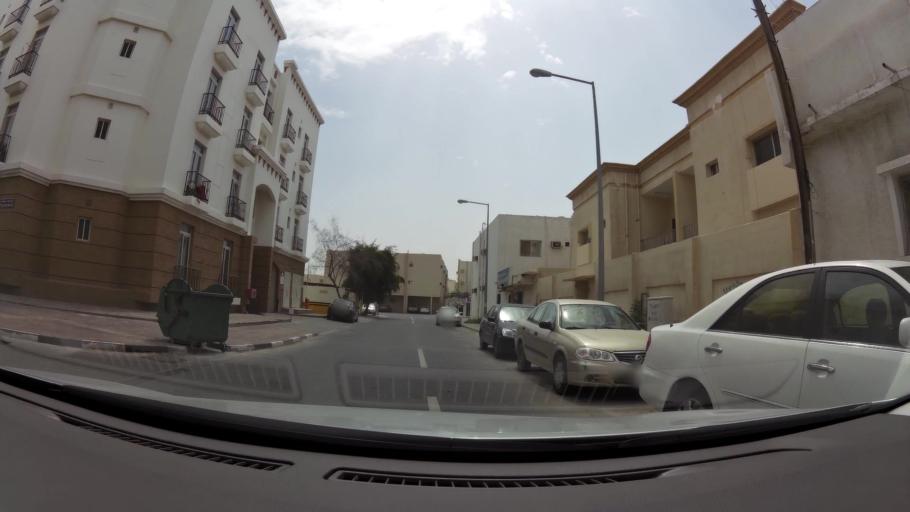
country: QA
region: Baladiyat ar Rayyan
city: Ar Rayyan
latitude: 25.3186
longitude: 51.4718
